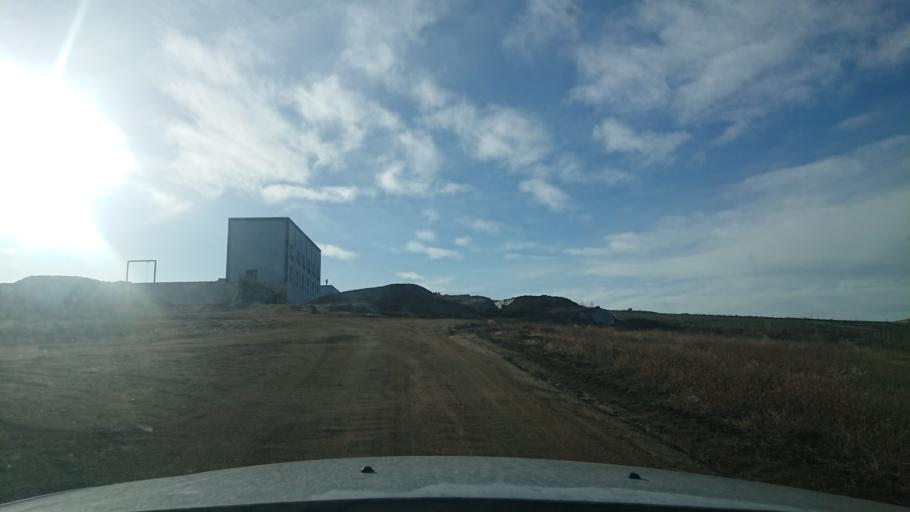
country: TR
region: Aksaray
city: Agacoren
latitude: 38.8473
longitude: 33.9432
